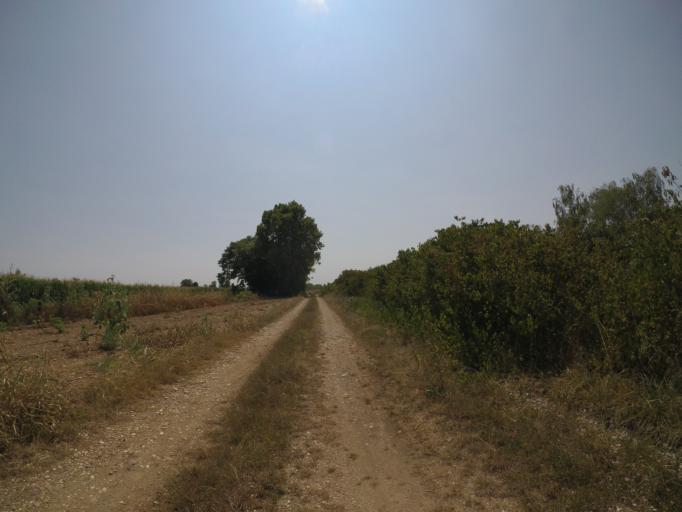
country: IT
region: Friuli Venezia Giulia
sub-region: Provincia di Udine
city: Mortegliano
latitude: 45.9373
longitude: 13.1653
